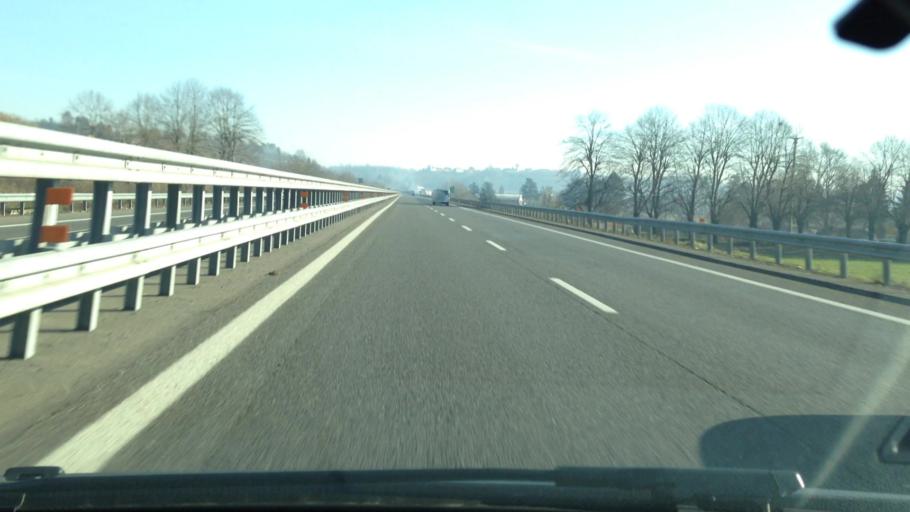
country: IT
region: Piedmont
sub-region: Provincia di Asti
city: Azzano d'Asti
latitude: 44.9096
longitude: 8.2643
